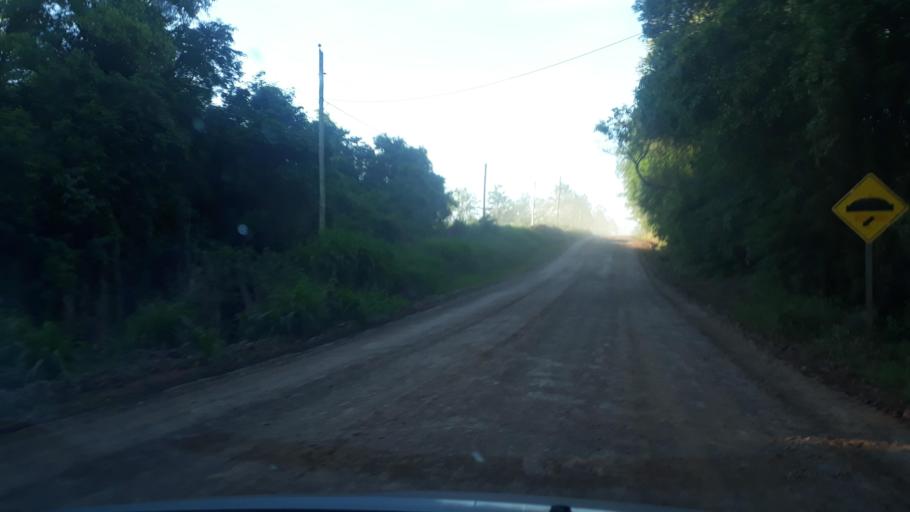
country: AR
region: Misiones
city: Ruiz de Montoya
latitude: -27.0543
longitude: -55.0046
